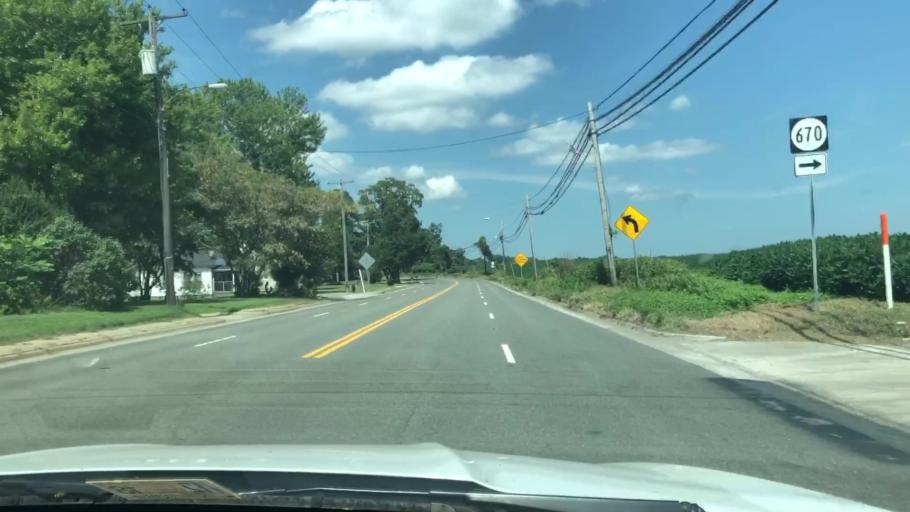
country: US
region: Virginia
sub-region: Richmond County
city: Warsaw
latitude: 37.9539
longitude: -76.7500
